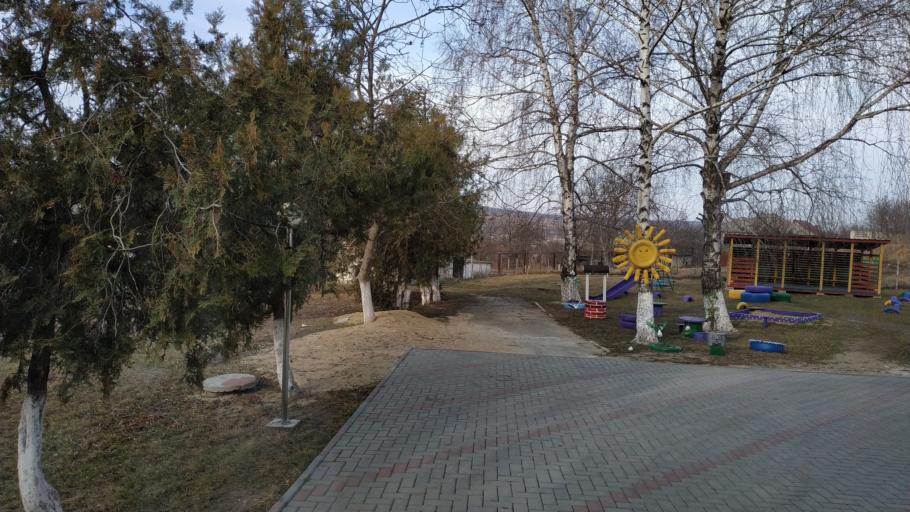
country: MD
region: Chisinau
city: Vatra
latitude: 46.9824
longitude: 28.6765
